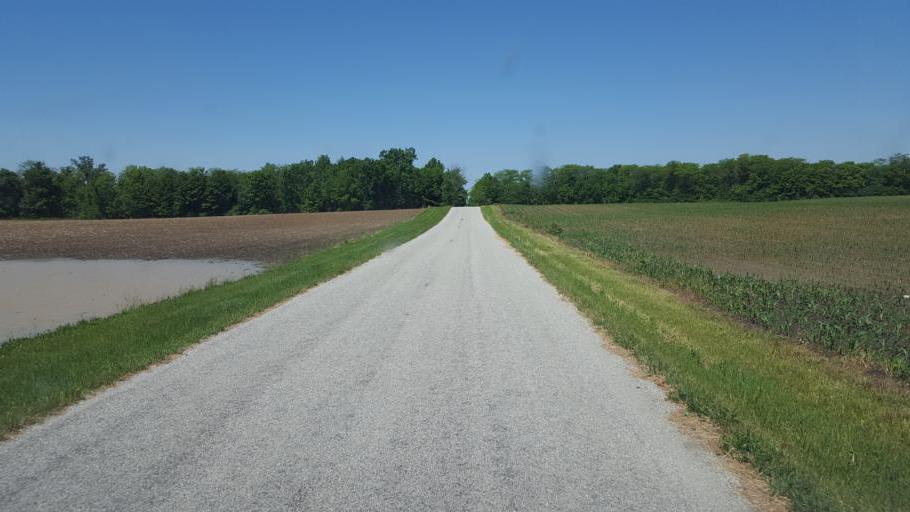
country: US
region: Ohio
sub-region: Hardin County
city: Forest
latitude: 40.6727
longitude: -83.3967
